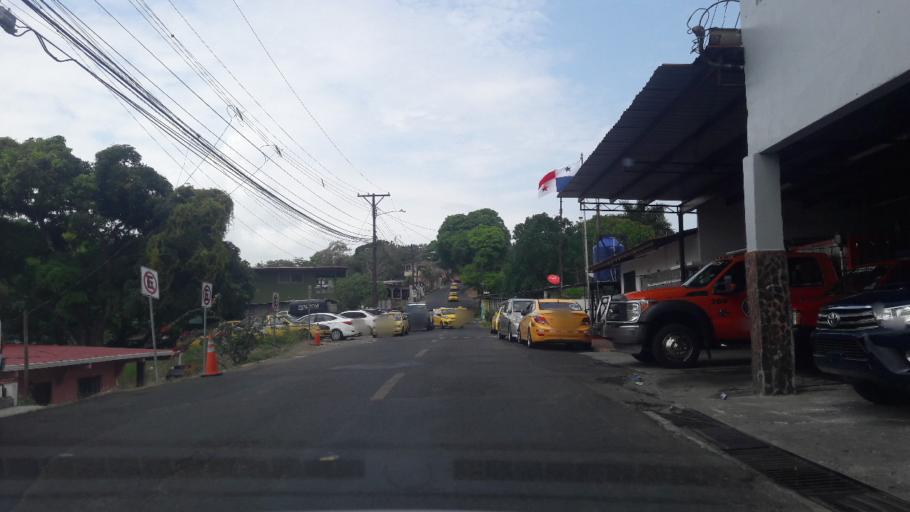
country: PA
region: Panama
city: Alcalde Diaz
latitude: 9.1187
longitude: -79.5552
